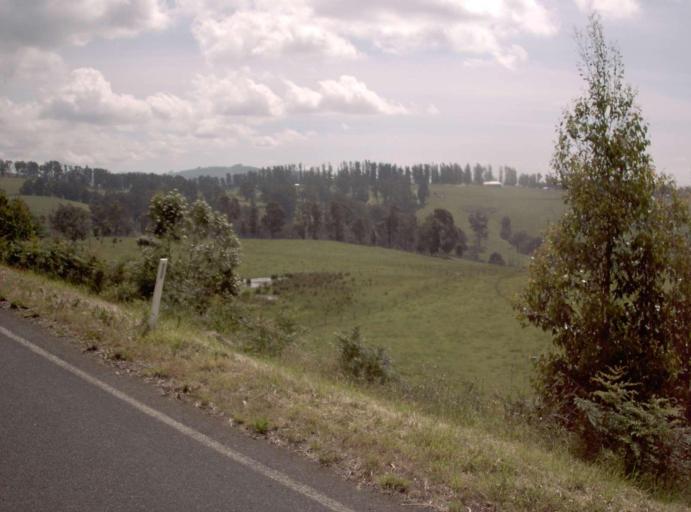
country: AU
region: Victoria
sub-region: Latrobe
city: Traralgon
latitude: -38.3449
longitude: 146.5697
